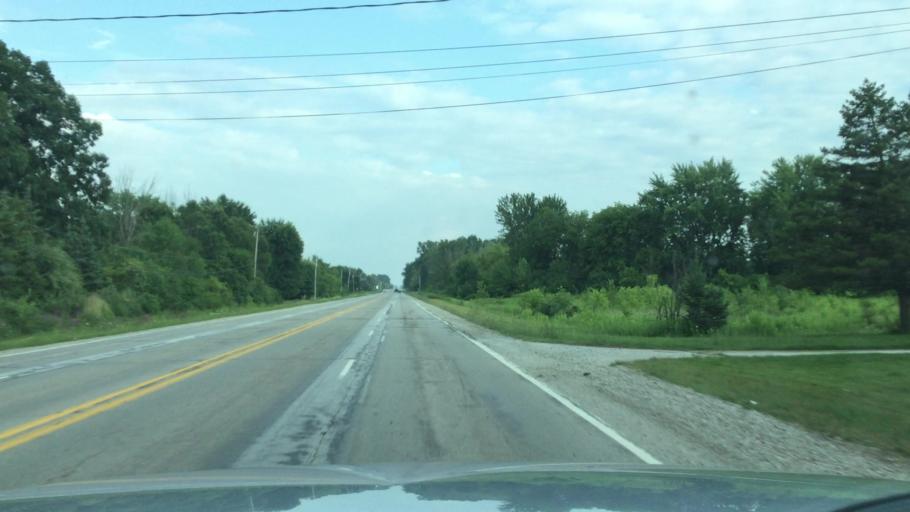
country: US
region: Michigan
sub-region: Saginaw County
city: Birch Run
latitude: 43.2751
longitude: -83.7882
